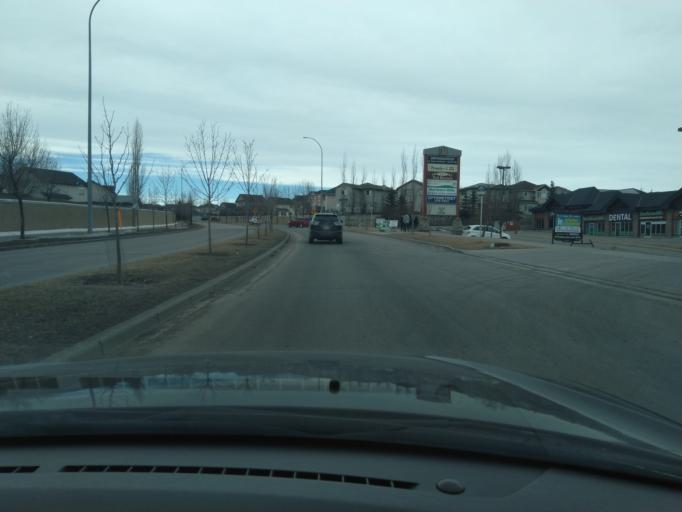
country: CA
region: Alberta
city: Calgary
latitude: 51.1646
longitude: -114.0712
